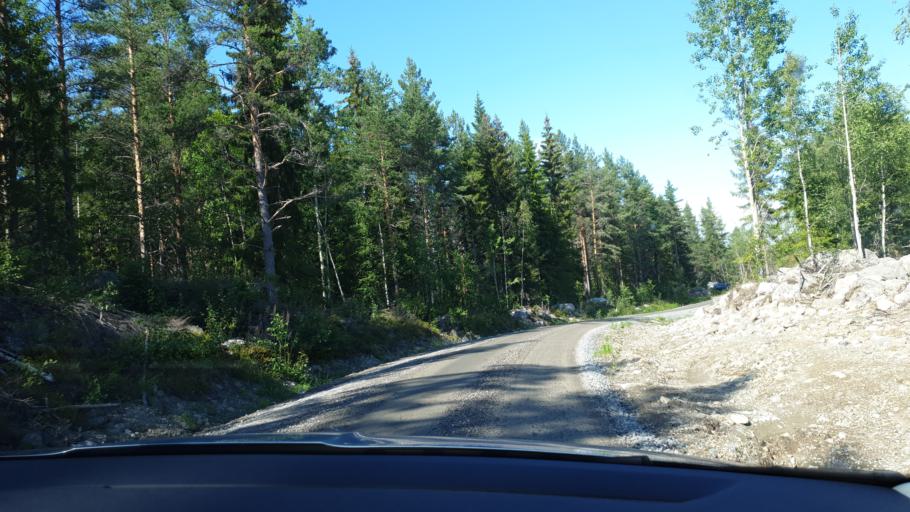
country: SE
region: Gaevleborg
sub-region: Soderhamns Kommun
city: Marielund
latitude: 61.4552
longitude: 17.0678
